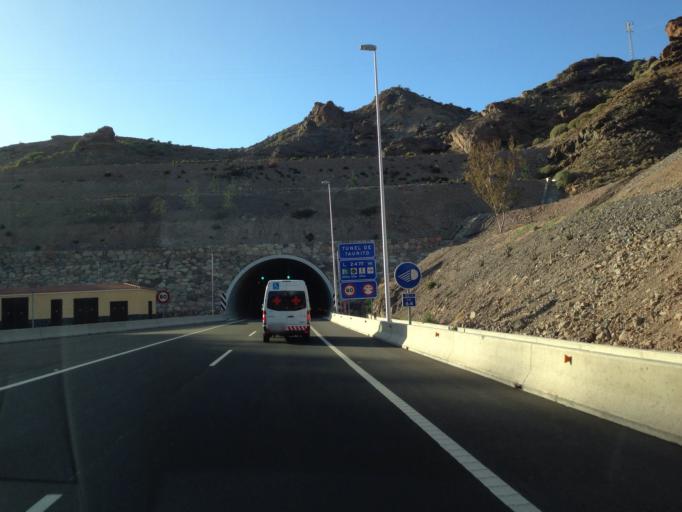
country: ES
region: Canary Islands
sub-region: Provincia de Las Palmas
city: Puerto Rico
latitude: 27.8100
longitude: -15.7263
